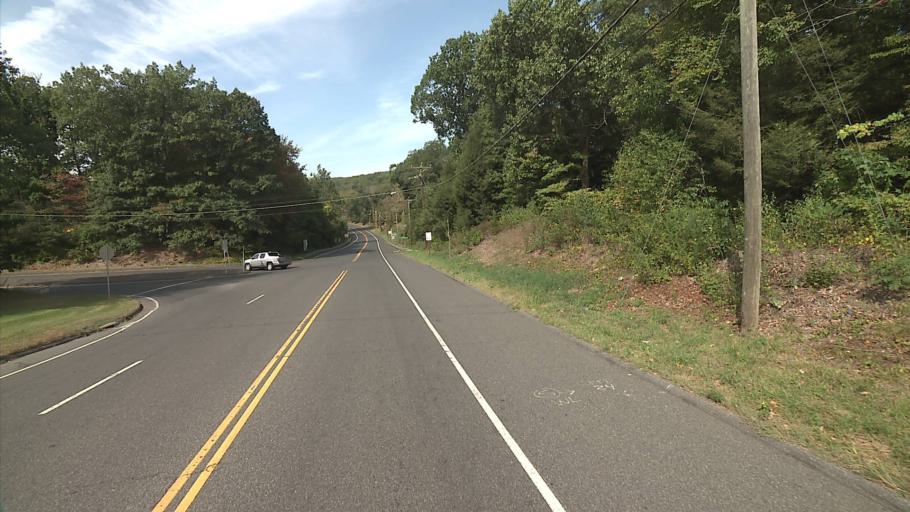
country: US
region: Connecticut
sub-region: New Haven County
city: Oxford
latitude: 41.3881
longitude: -73.1876
